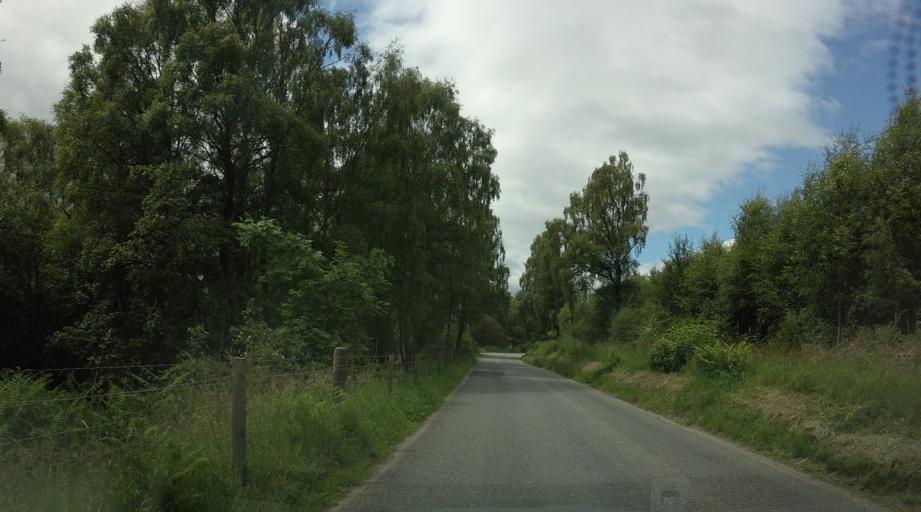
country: GB
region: Scotland
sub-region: Perth and Kinross
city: Aberfeldy
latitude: 56.7189
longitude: -3.8923
